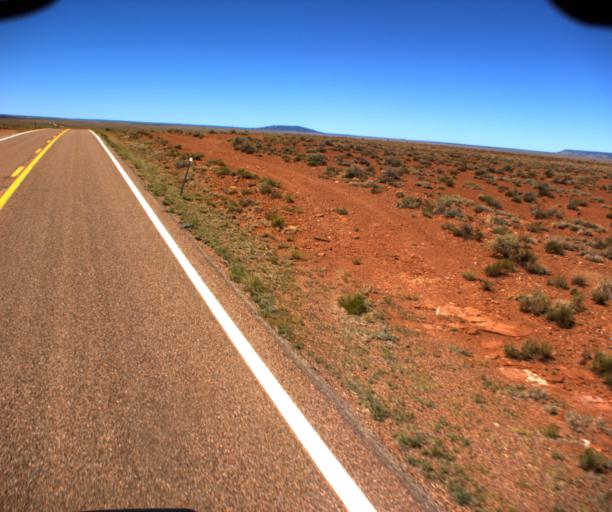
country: US
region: Arizona
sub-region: Navajo County
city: Winslow
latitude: 34.8640
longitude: -110.6599
